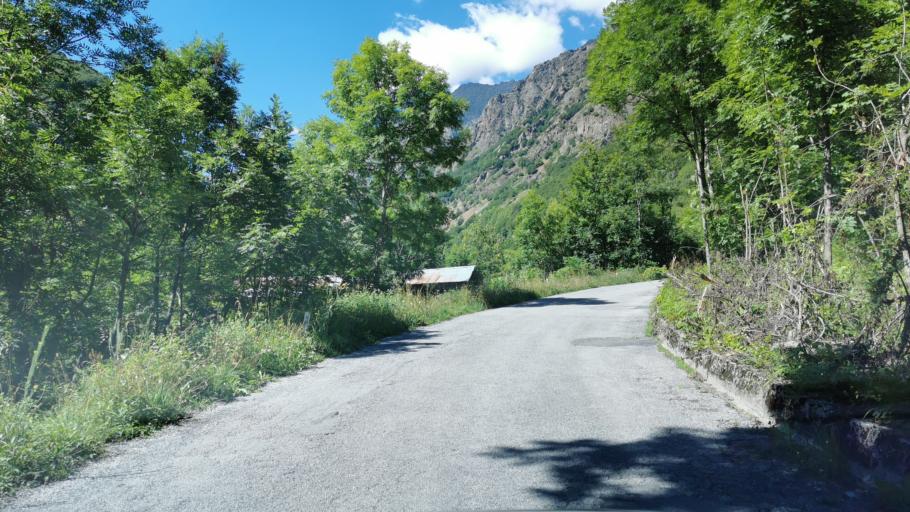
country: IT
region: Piedmont
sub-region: Provincia di Cuneo
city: Entracque
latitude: 44.2080
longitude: 7.3781
